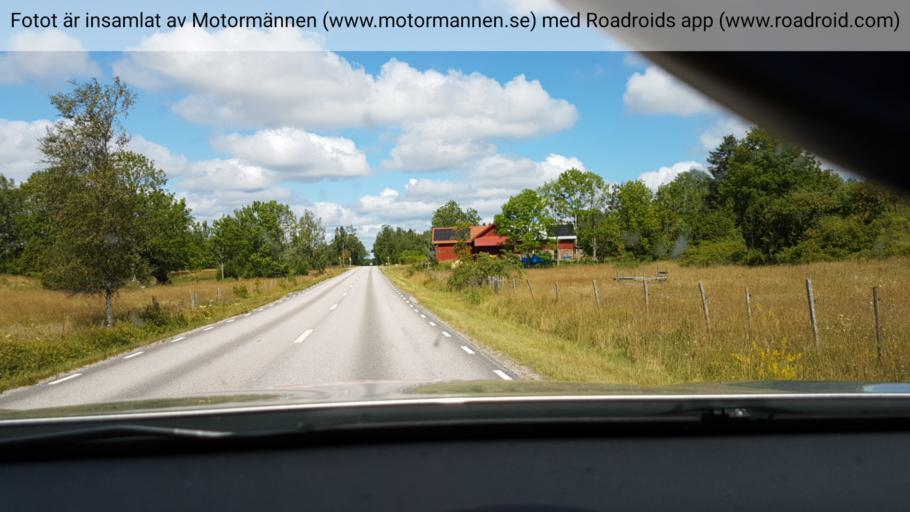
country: SE
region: Stockholm
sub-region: Norrtalje Kommun
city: Arno
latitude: 60.0289
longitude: 18.7867
